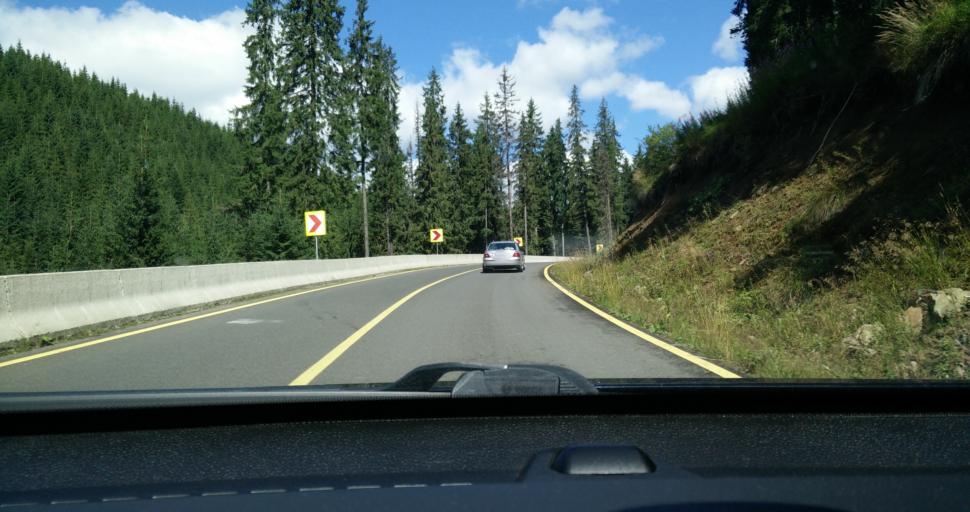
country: RO
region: Hunedoara
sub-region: Oras Petrila
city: Petrila
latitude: 45.4422
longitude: 23.6250
